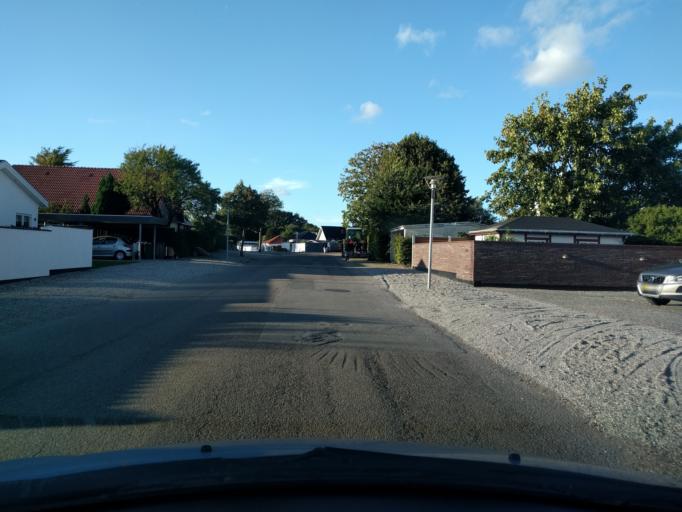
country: DK
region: South Denmark
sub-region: Nyborg Kommune
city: Nyborg
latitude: 55.3272
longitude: 10.8080
